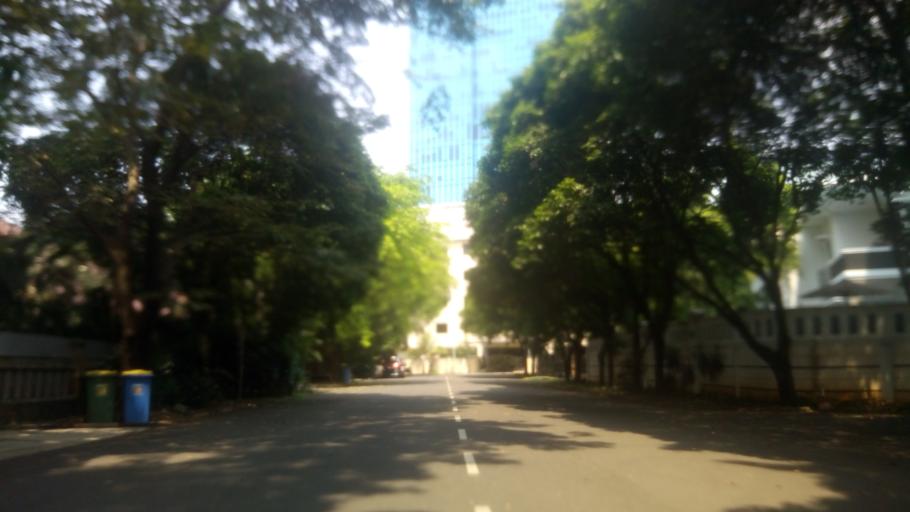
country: ID
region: Jakarta Raya
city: Jakarta
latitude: -6.2388
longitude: 106.8343
